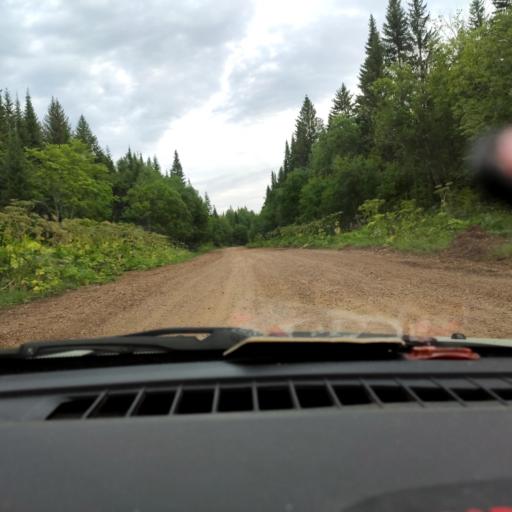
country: RU
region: Perm
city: Kultayevo
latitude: 57.8131
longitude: 56.0026
